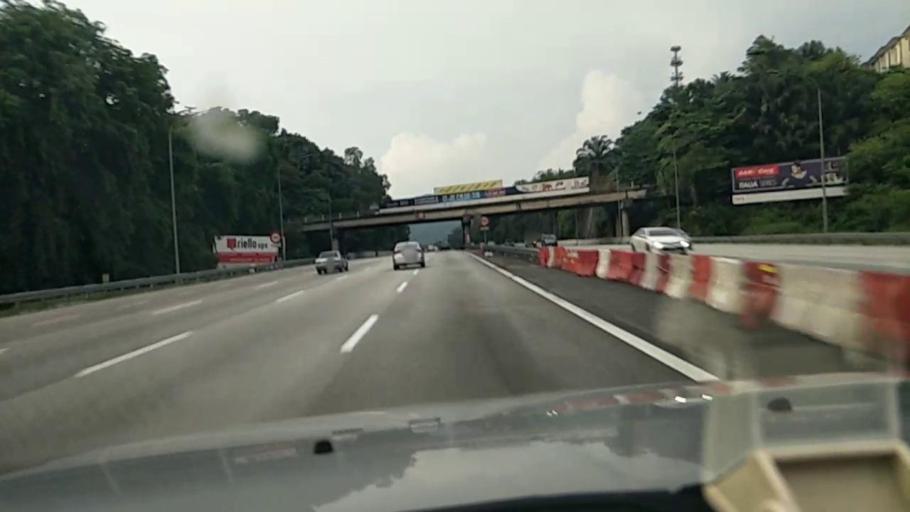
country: MY
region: Selangor
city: Kuang
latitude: 3.2062
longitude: 101.5828
